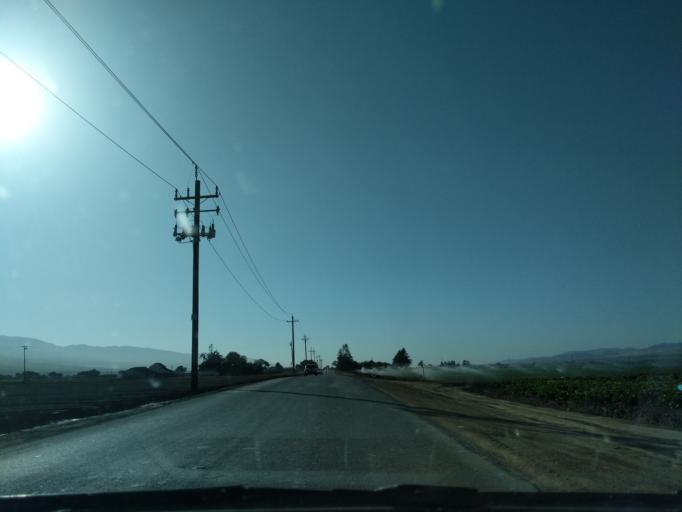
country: US
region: California
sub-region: Monterey County
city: Soledad
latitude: 36.3971
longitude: -121.3357
